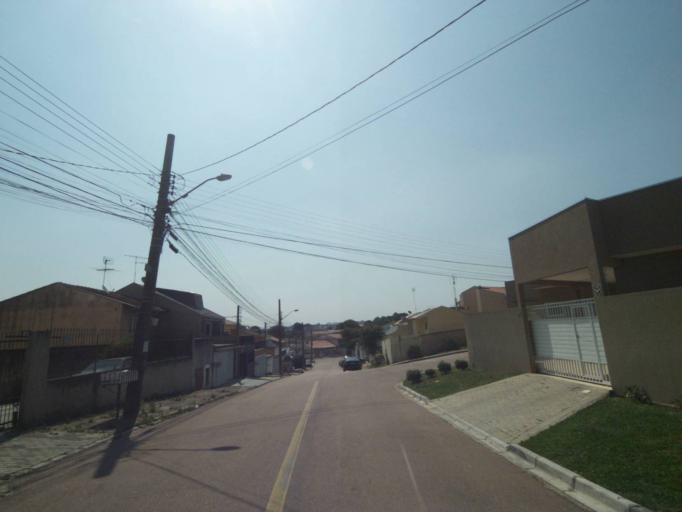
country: BR
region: Parana
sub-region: Curitiba
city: Curitiba
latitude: -25.4829
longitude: -49.3218
